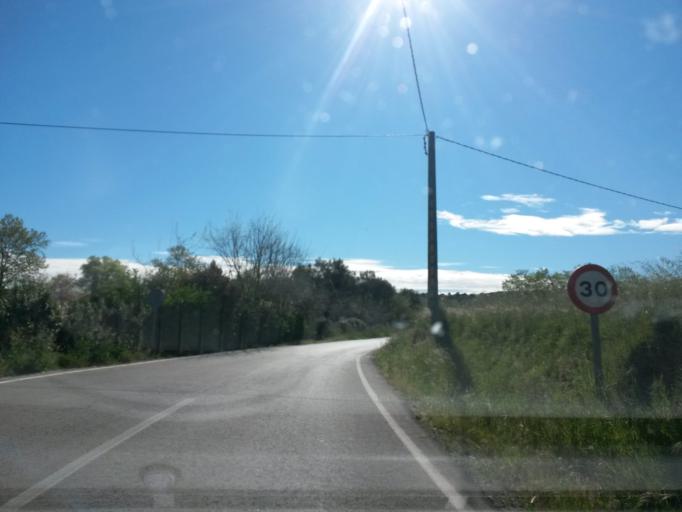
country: ES
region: Catalonia
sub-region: Provincia de Girona
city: Juia
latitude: 42.0224
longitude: 2.9064
